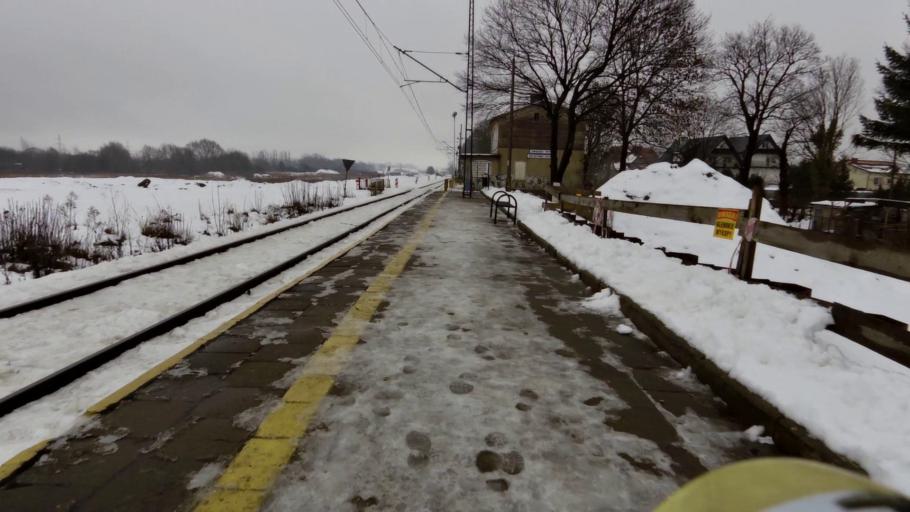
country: PL
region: West Pomeranian Voivodeship
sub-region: Powiat szczecinecki
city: Szczecinek
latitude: 53.7183
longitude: 16.6970
